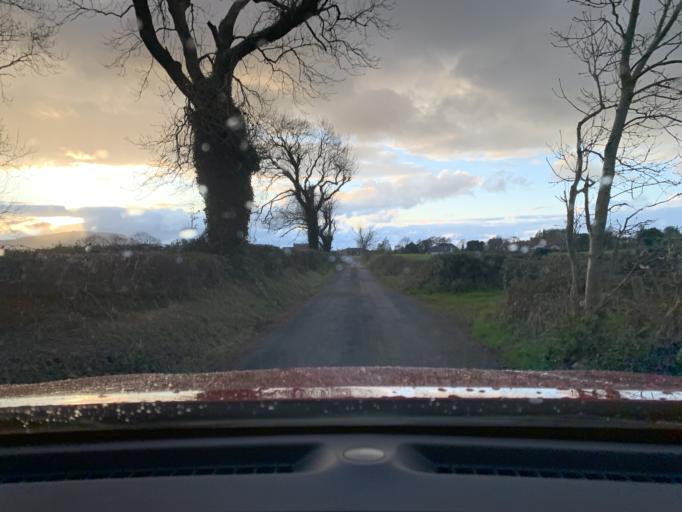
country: IE
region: Connaught
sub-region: Sligo
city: Sligo
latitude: 54.2953
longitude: -8.4887
